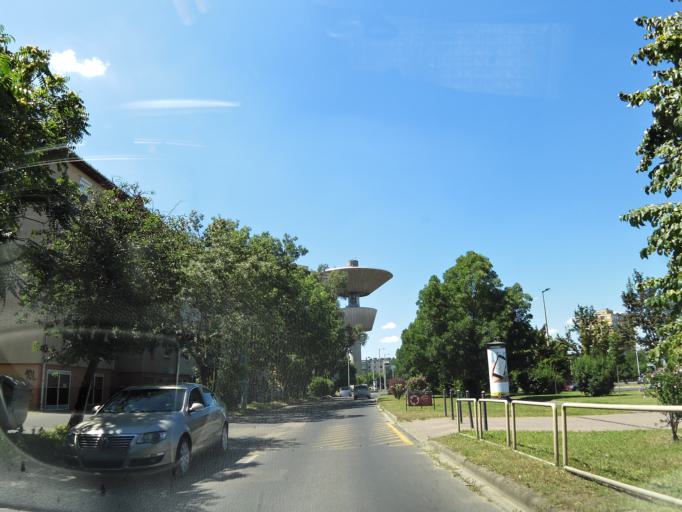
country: HU
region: Csongrad
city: Szeged
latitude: 46.2676
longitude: 20.1375
